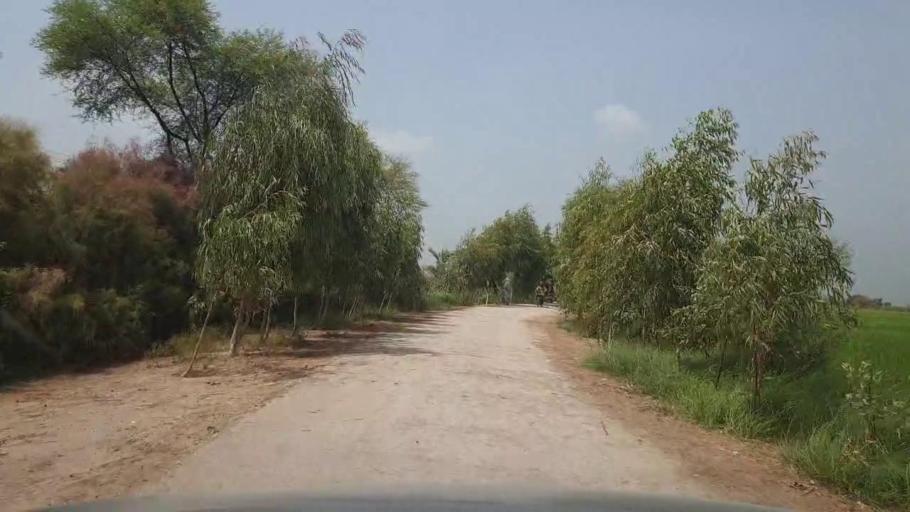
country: PK
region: Sindh
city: Garhi Yasin
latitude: 27.9460
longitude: 68.3746
